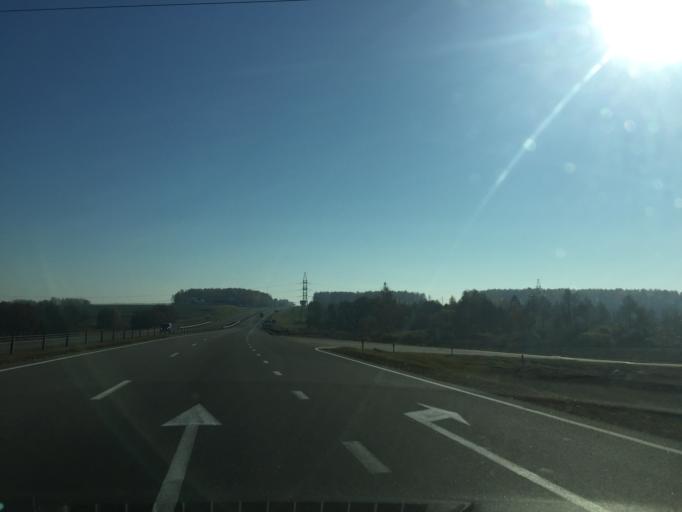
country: BY
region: Mogilev
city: Buynichy
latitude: 53.9601
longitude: 30.1963
